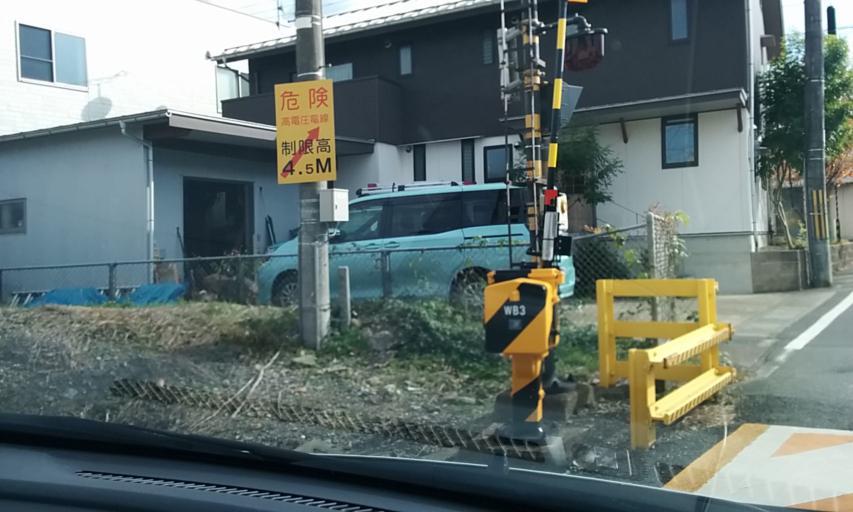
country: JP
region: Kyoto
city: Fukuchiyama
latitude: 35.3004
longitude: 135.1785
